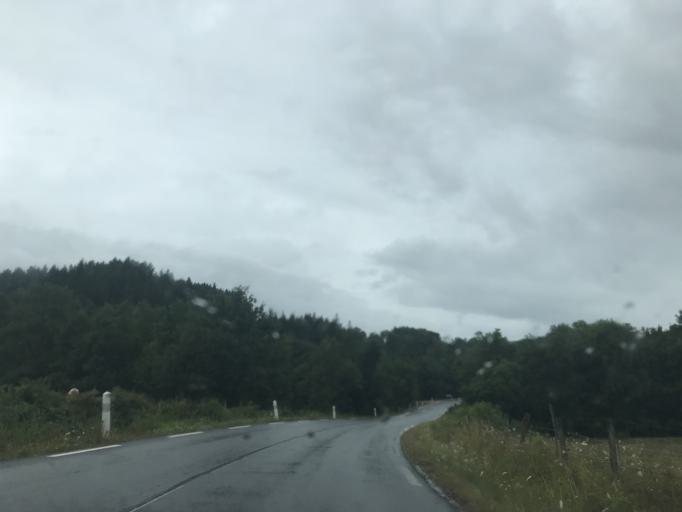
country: FR
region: Auvergne
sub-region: Departement du Puy-de-Dome
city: Job
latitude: 45.5866
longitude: 3.7279
